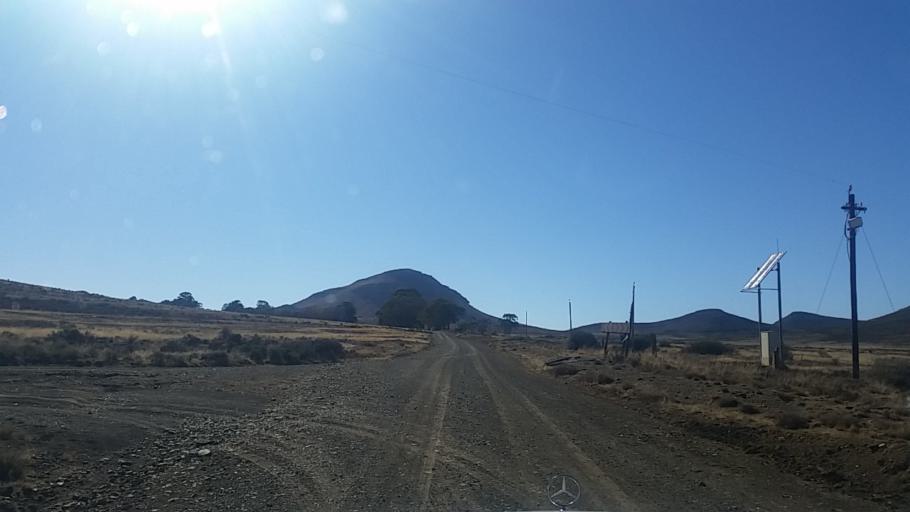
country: ZA
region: Eastern Cape
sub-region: Chris Hani District Municipality
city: Middelburg
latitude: -31.7983
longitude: 24.7251
